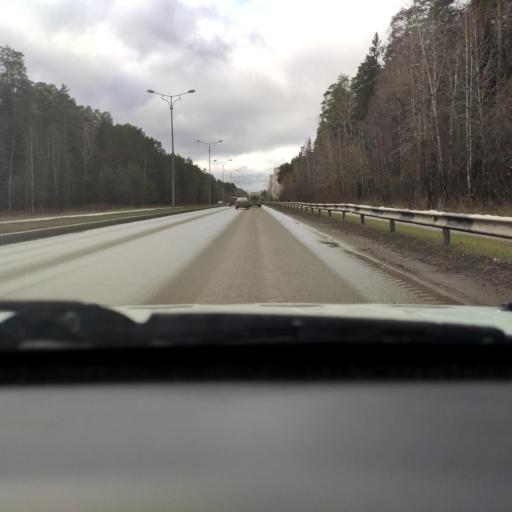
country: RU
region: Perm
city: Kondratovo
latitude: 58.0187
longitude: 55.9898
